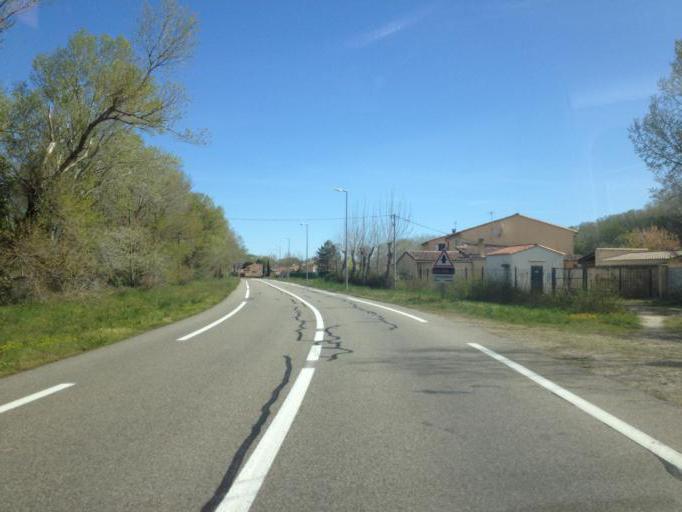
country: FR
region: Provence-Alpes-Cote d'Azur
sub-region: Departement du Vaucluse
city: Caderousse
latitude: 44.0927
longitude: 4.7410
